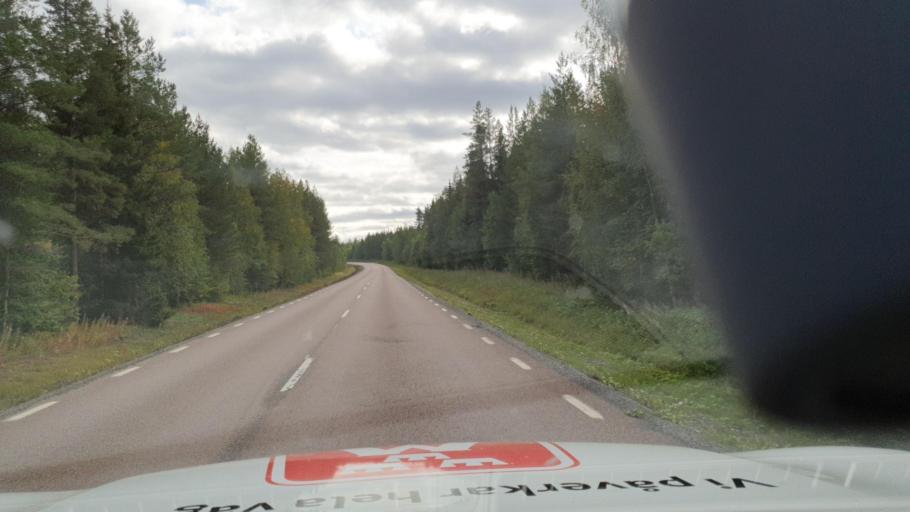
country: SE
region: Jaemtland
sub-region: Stroemsunds Kommun
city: Stroemsund
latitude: 63.7495
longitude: 15.7236
